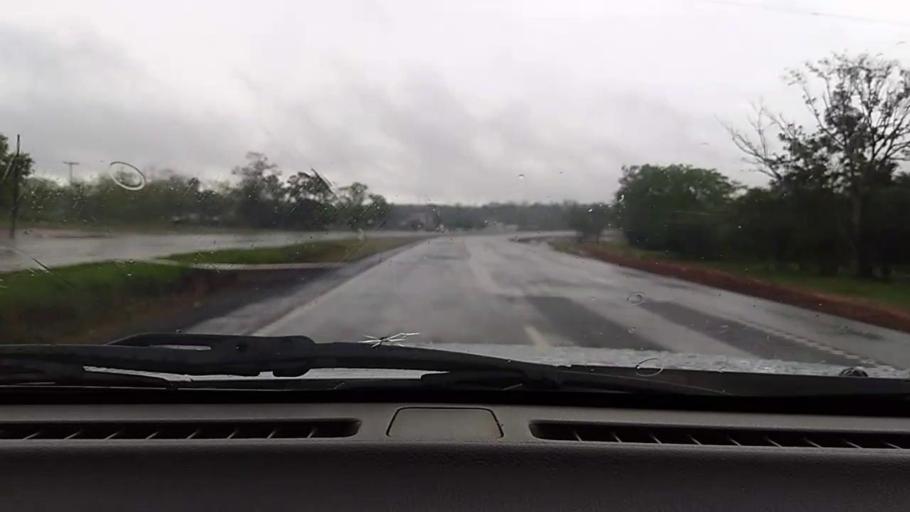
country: PY
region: Caaguazu
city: Repatriacion
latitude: -25.4651
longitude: -55.9323
